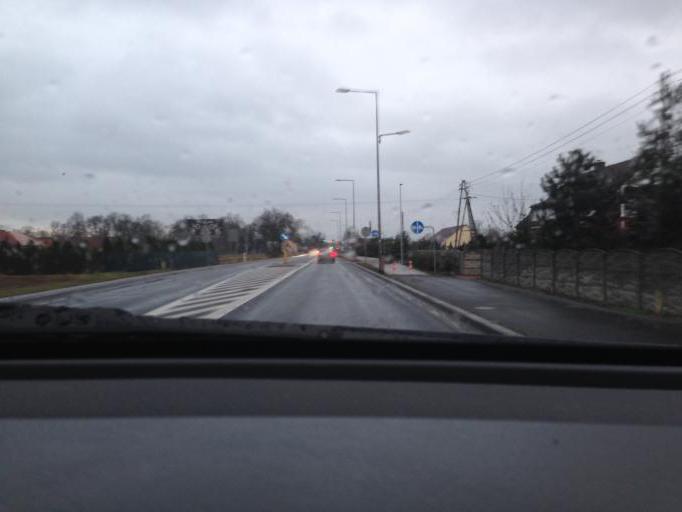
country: PL
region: Opole Voivodeship
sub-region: Powiat opolski
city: Wegry
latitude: 50.7161
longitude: 17.9973
